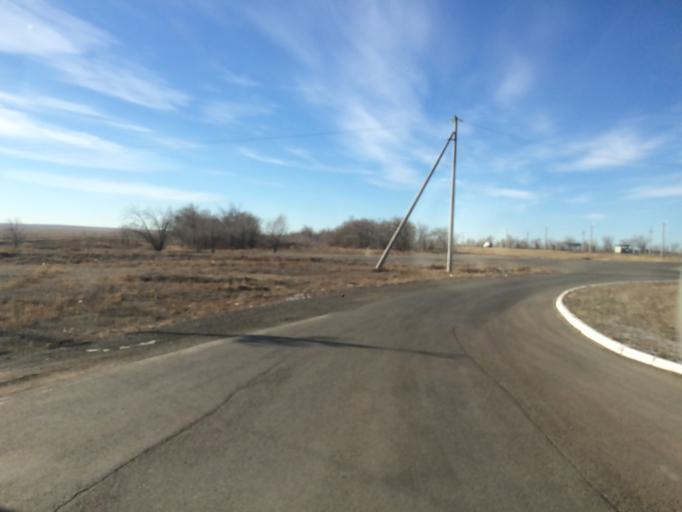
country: KZ
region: Aqtoebe
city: Aqtobe
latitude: 50.2634
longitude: 56.9543
